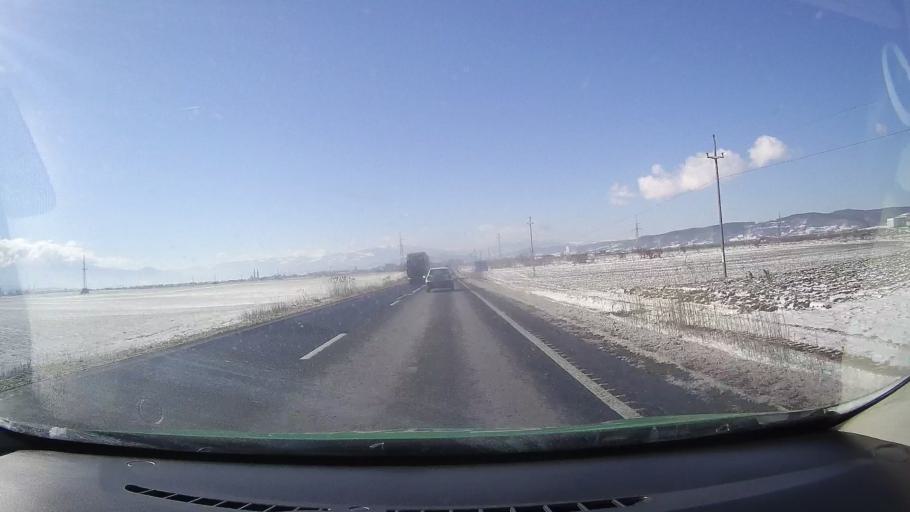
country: RO
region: Sibiu
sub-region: Comuna Avrig
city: Avrig
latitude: 45.7398
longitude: 24.3975
